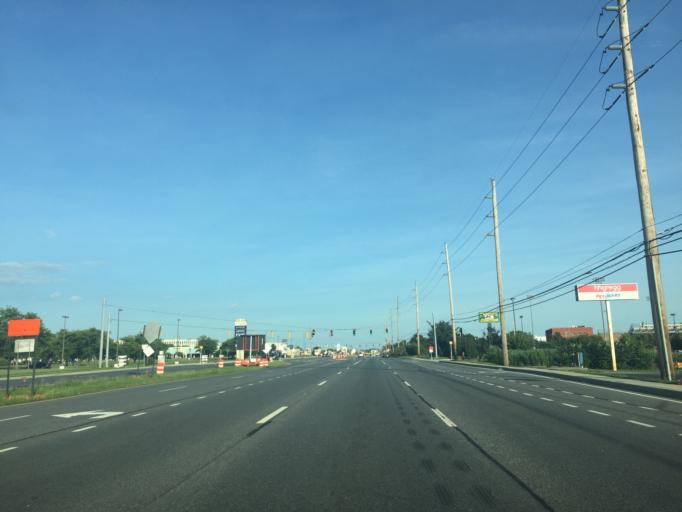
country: US
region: Delaware
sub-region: Kent County
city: Dover
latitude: 39.1917
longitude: -75.5443
